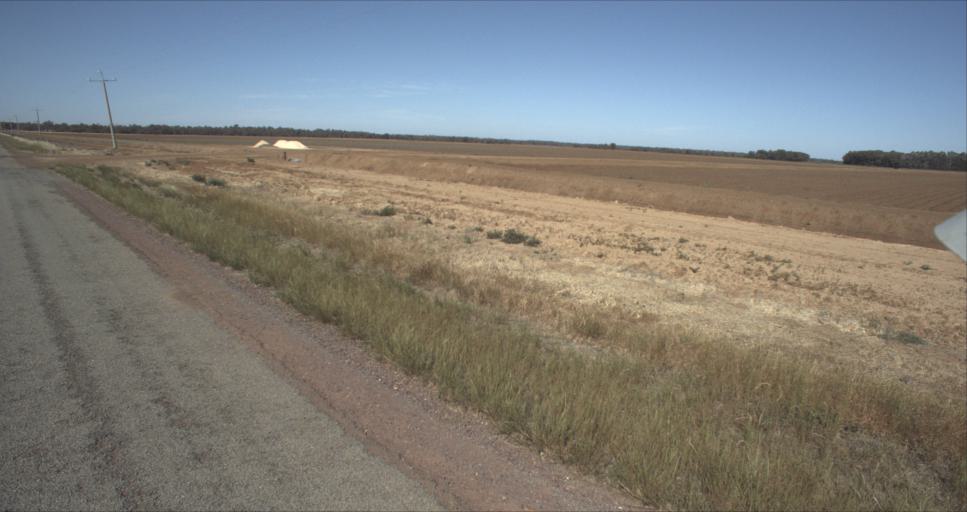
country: AU
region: New South Wales
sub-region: Leeton
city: Leeton
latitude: -34.5936
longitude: 146.2591
